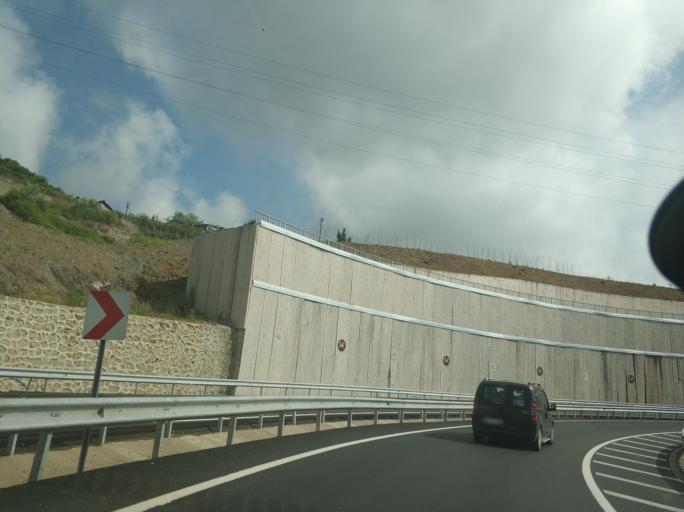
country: TR
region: Ordu
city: Ordu
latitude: 40.9532
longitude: 37.9043
